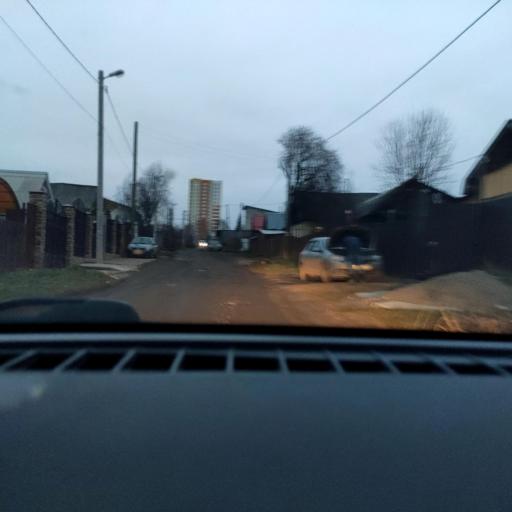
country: RU
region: Perm
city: Kondratovo
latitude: 57.9625
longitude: 56.1486
